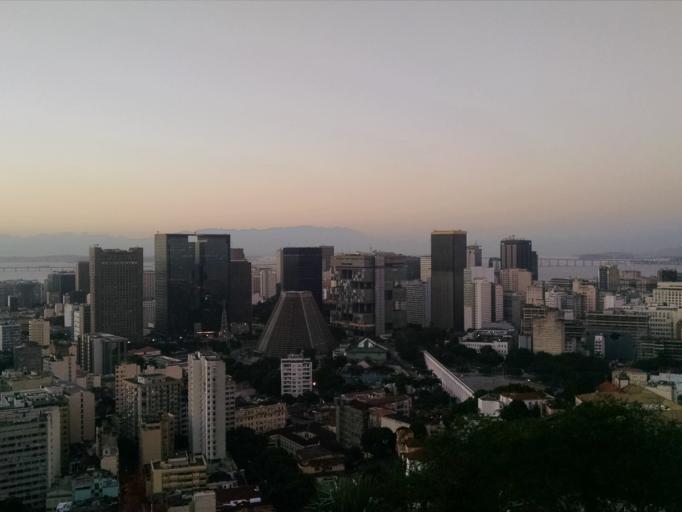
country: BR
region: Rio de Janeiro
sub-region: Rio De Janeiro
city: Rio de Janeiro
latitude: -22.9179
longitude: -43.1824
